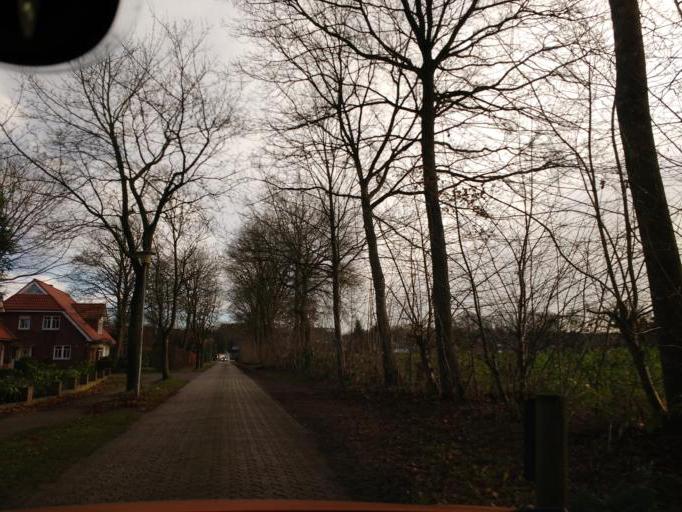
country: DE
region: Lower Saxony
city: Hude
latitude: 53.1057
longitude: 8.4535
